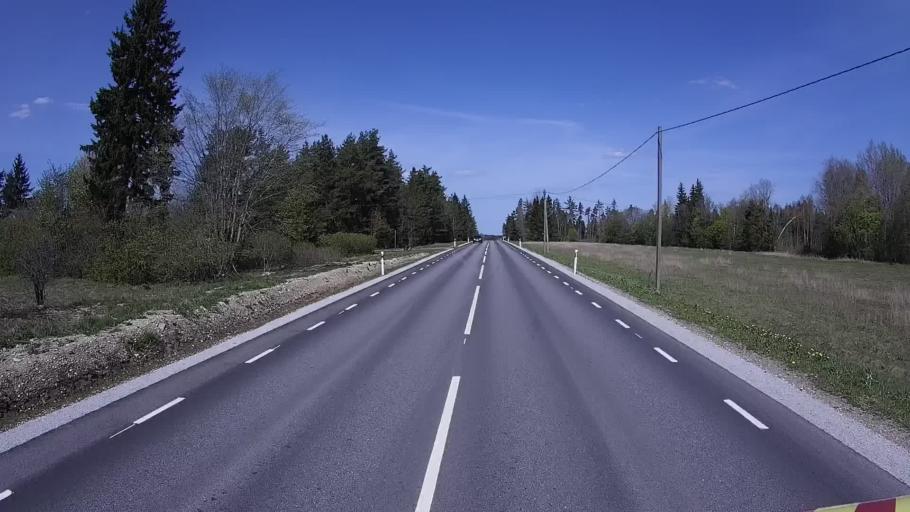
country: EE
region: Harju
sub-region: Paldiski linn
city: Paldiski
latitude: 59.2017
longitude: 24.0967
